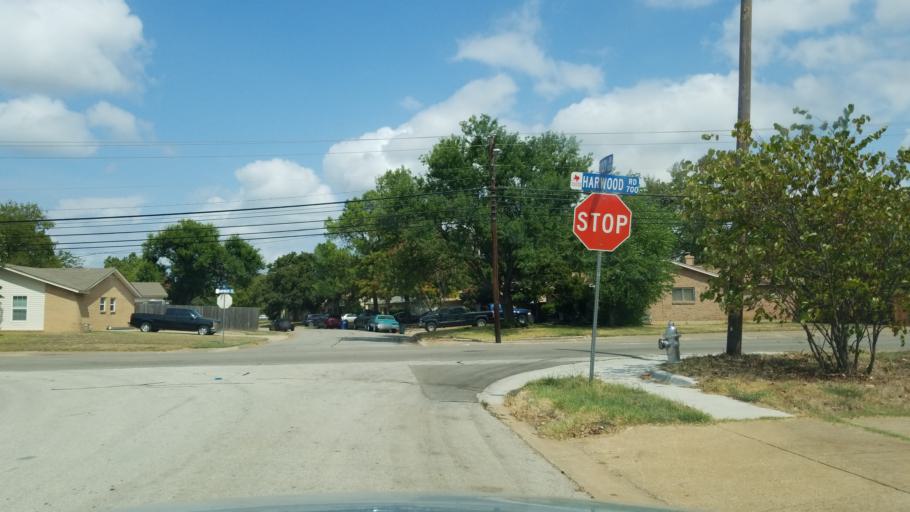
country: US
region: Texas
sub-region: Tarrant County
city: Euless
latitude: 32.8515
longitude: -97.0936
